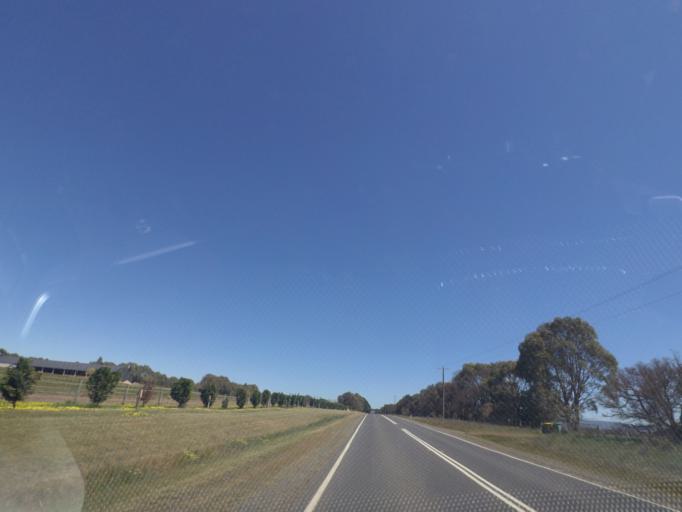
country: AU
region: Victoria
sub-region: Hume
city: Sunbury
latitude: -37.2849
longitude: 144.7698
